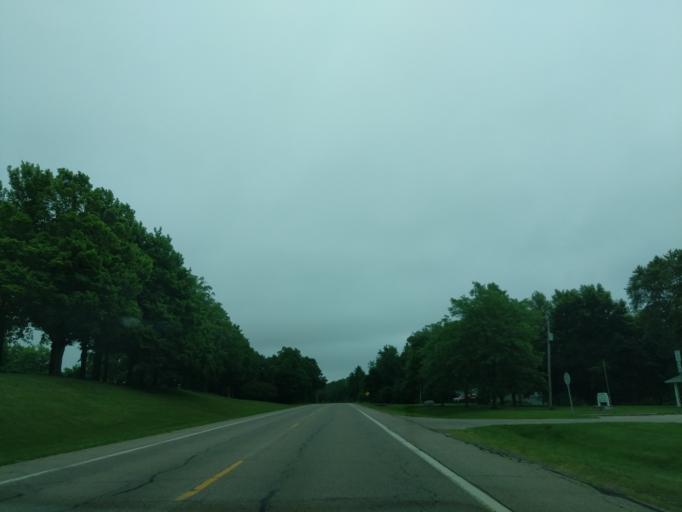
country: US
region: Michigan
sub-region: Hillsdale County
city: Litchfield
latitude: 42.0341
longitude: -84.7351
